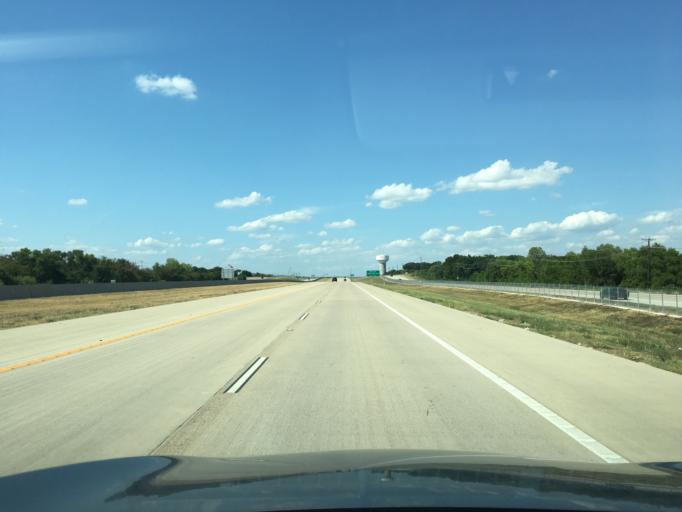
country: US
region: Texas
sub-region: Tarrant County
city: Mansfield
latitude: 32.5936
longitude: -97.0775
